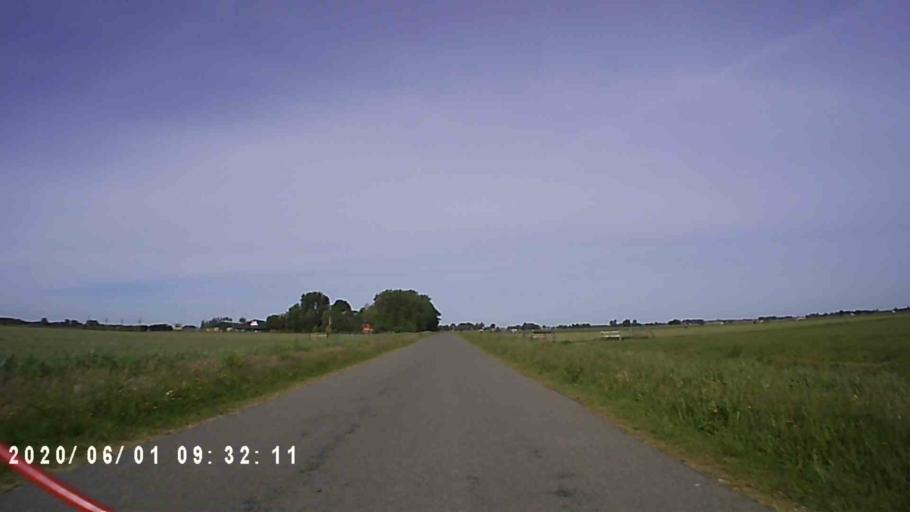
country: NL
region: Friesland
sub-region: Gemeente Leeuwarderadeel
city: Stiens
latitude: 53.2624
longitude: 5.7297
